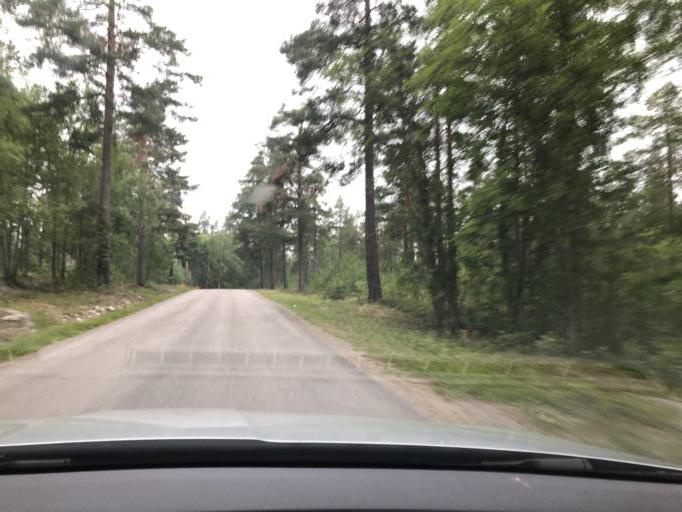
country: SE
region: Vaesternorrland
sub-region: Sundsvalls Kommun
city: Sundsvall
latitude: 62.4010
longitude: 17.3091
